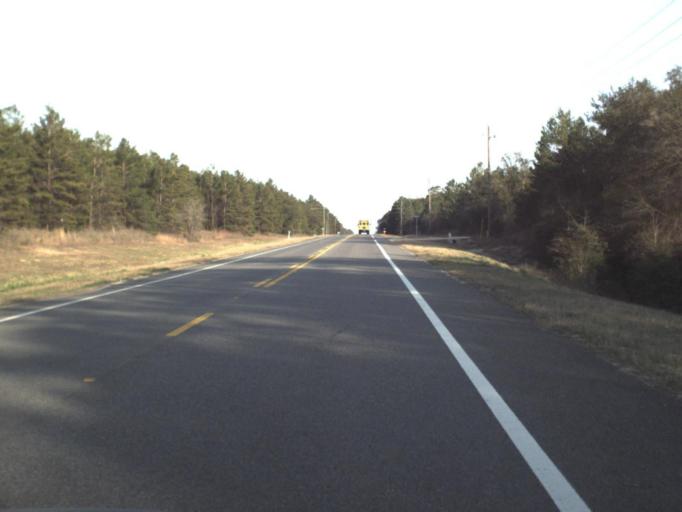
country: US
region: Florida
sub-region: Bay County
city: Lynn Haven
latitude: 30.4294
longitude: -85.6806
